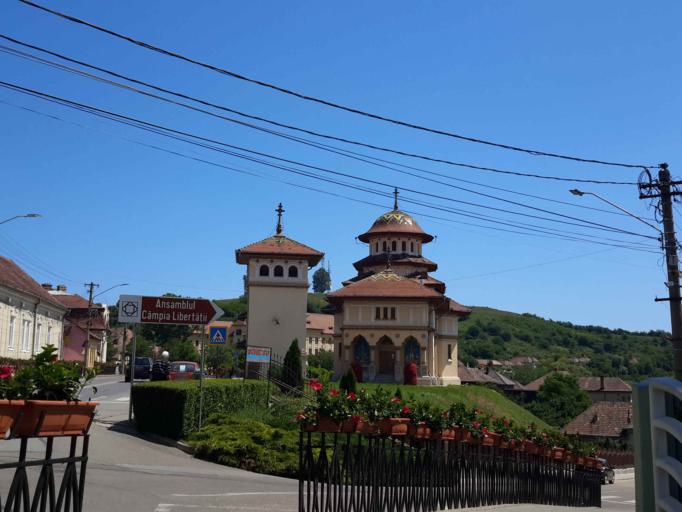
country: RO
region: Alba
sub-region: Municipiul Blaj
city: Blaj
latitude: 46.1763
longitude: 23.9242
